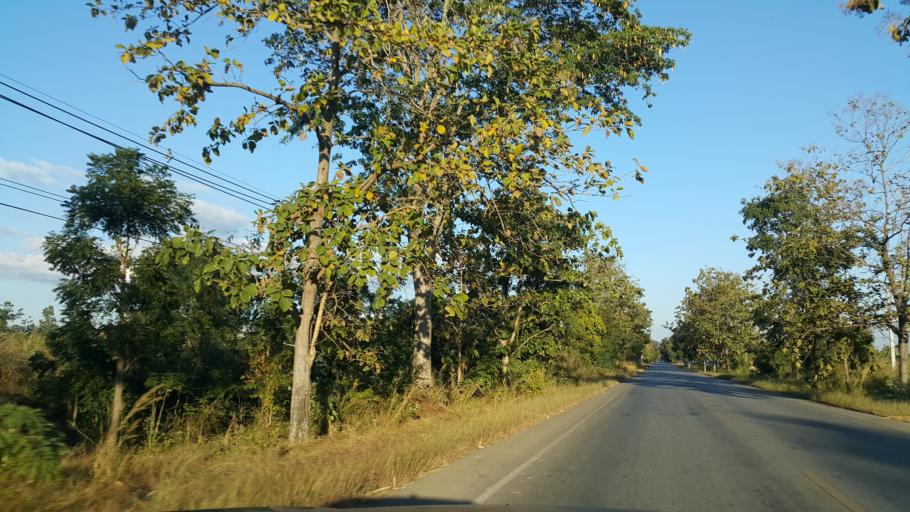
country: TH
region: Sukhothai
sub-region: Amphoe Si Satchanalai
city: Si Satchanalai
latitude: 17.5419
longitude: 99.8224
